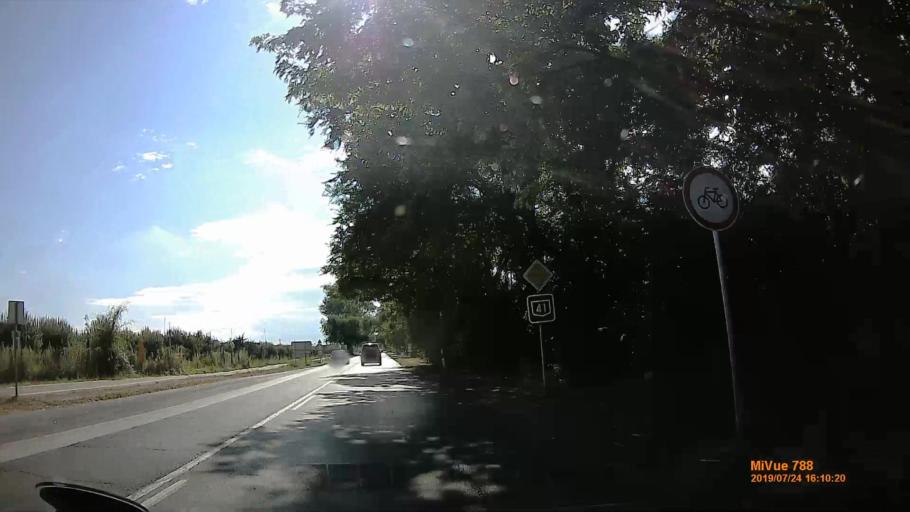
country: HU
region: Szabolcs-Szatmar-Bereg
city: Napkor
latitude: 47.9510
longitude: 21.8535
